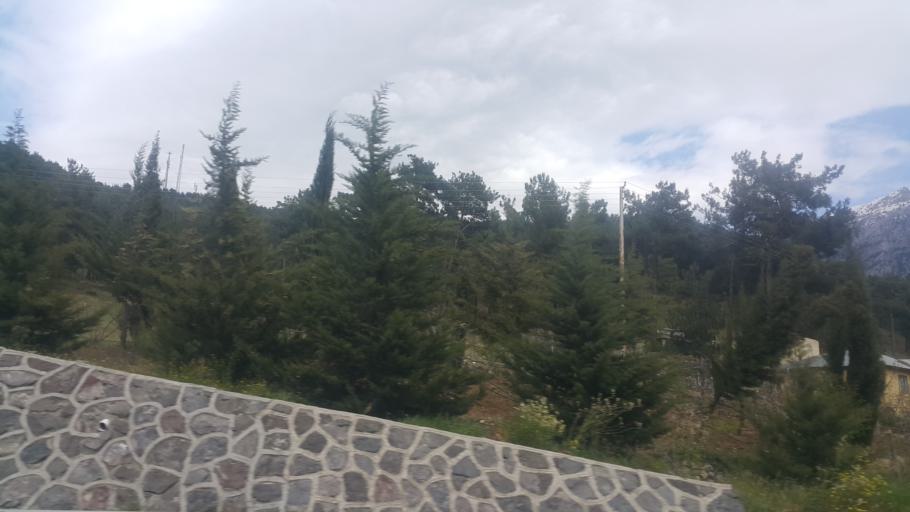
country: TR
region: Adana
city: Pozanti
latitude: 37.4192
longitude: 34.8774
